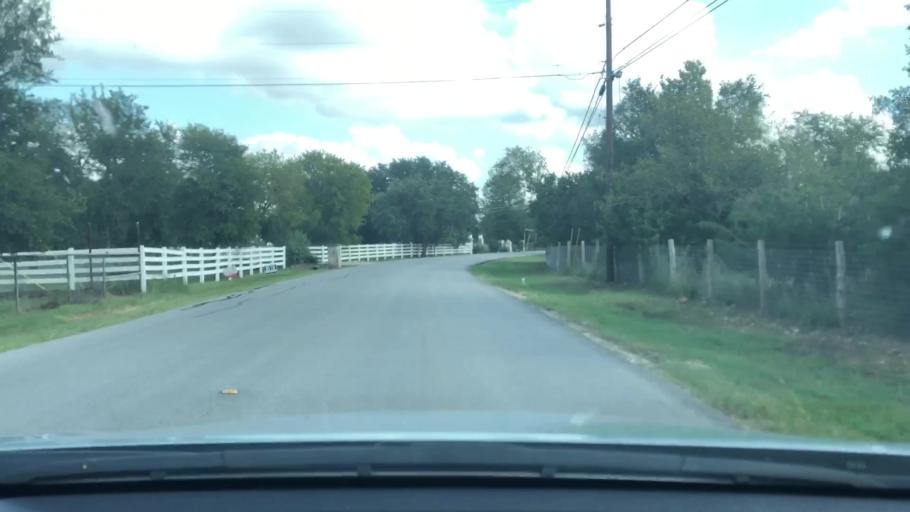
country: US
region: Texas
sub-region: Bexar County
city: Fair Oaks Ranch
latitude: 29.7621
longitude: -98.6270
